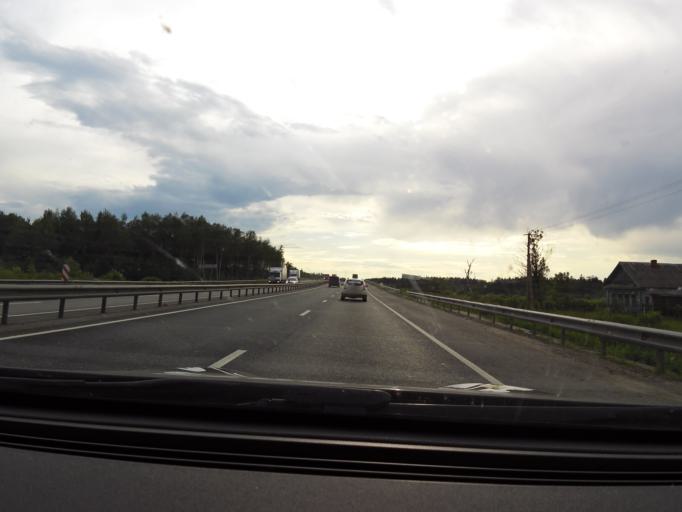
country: RU
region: Vladimir
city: Luknovo
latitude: 56.2375
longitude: 41.9844
